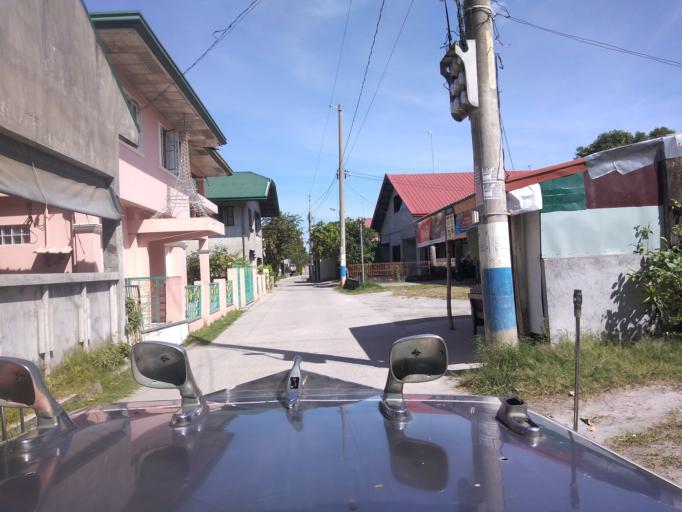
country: PH
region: Central Luzon
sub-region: Province of Pampanga
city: Magliman
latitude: 15.0267
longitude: 120.6563
